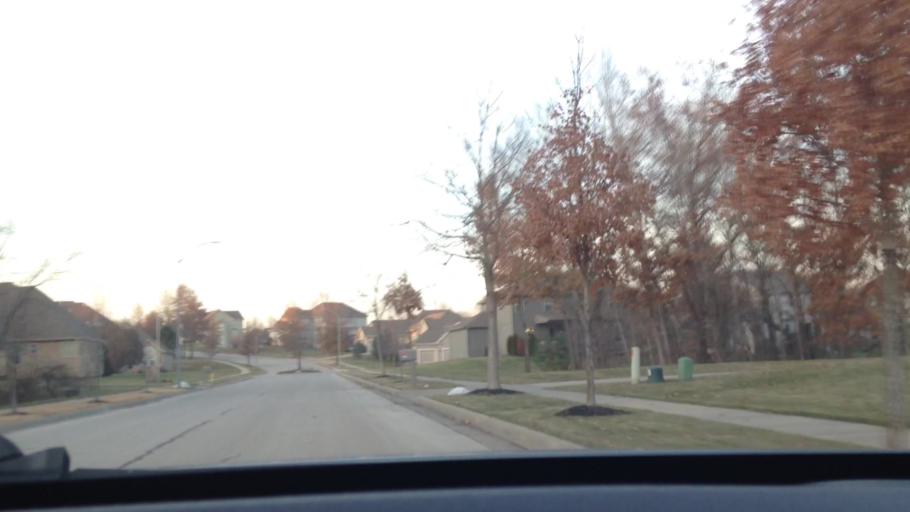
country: US
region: Missouri
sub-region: Clay County
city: Liberty
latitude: 39.2164
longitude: -94.4440
